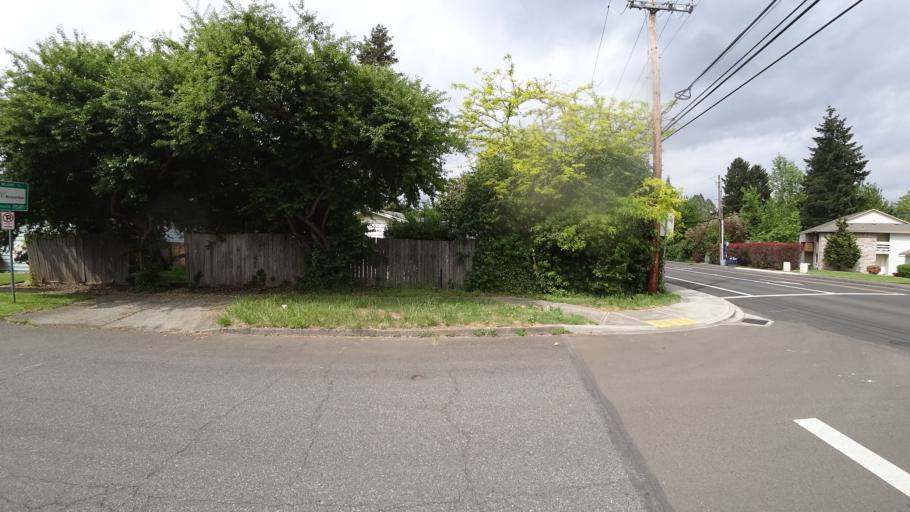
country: US
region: Oregon
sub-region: Washington County
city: Garden Home-Whitford
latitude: 45.4676
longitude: -122.7769
